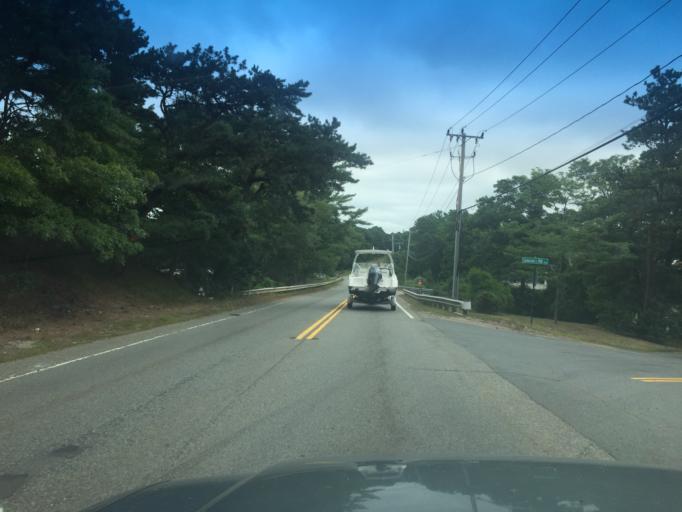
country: US
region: Massachusetts
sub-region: Barnstable County
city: Mashpee
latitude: 41.6306
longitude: -70.4677
